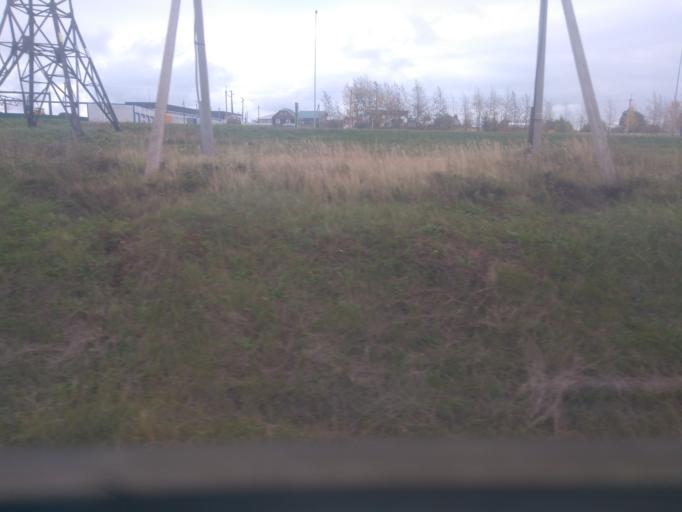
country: RU
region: Tatarstan
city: Mendeleyevsk
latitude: 55.8855
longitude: 52.3126
